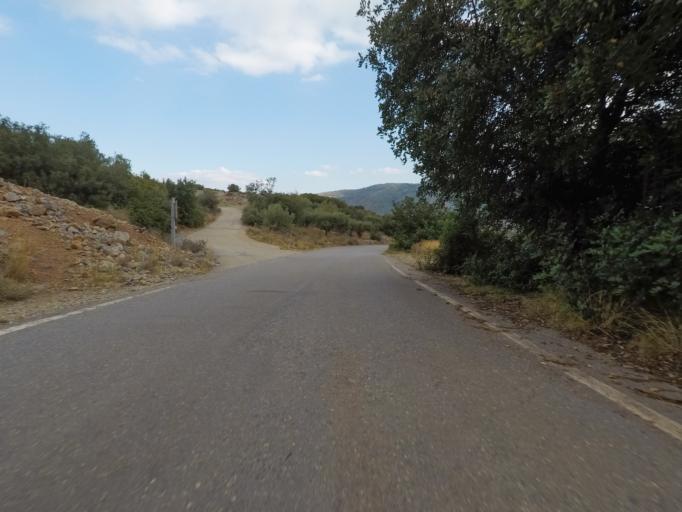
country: GR
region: Crete
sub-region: Nomos Lasithiou
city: Kritsa
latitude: 35.1669
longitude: 25.6556
